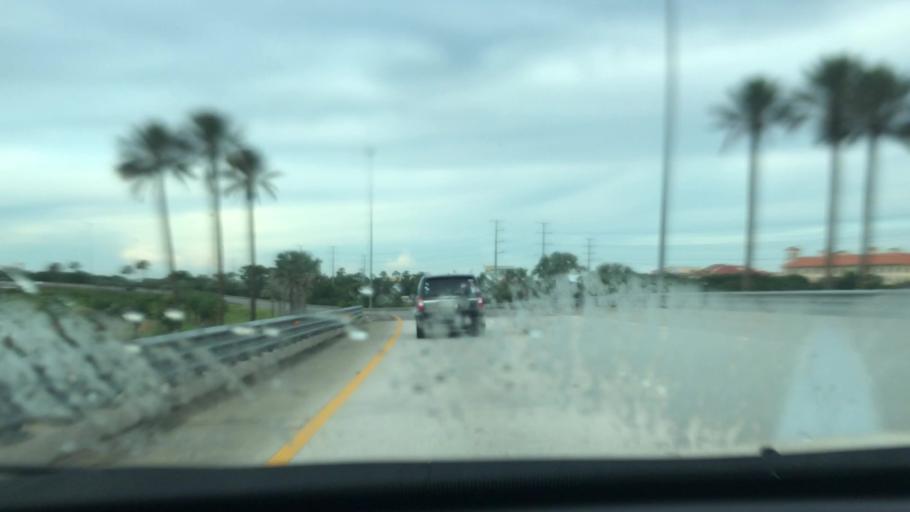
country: US
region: Florida
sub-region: Osceola County
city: Celebration
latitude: 28.3312
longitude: -81.5457
